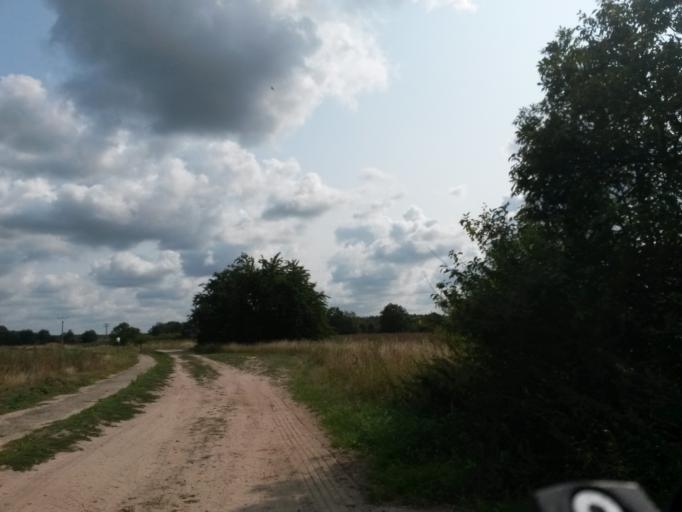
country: DE
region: Saxony-Anhalt
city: Klietz
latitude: 52.6564
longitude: 12.0451
